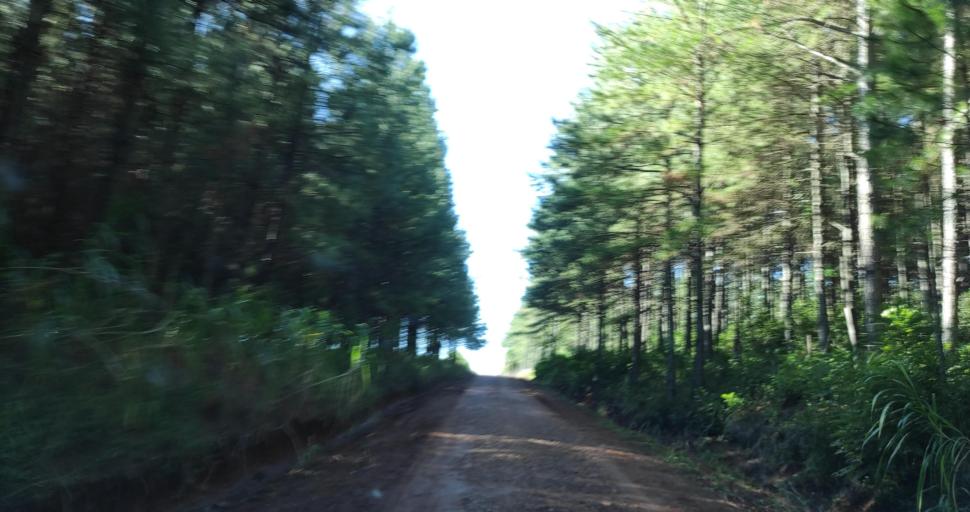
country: AR
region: Misiones
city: Capiovi
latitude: -26.9267
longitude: -55.0008
